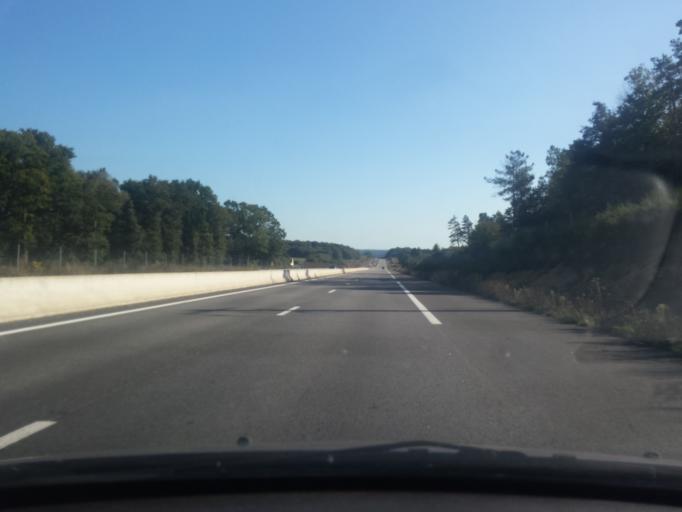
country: FR
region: Brittany
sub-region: Departement du Morbihan
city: Colpo
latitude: 47.8067
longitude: -2.8083
